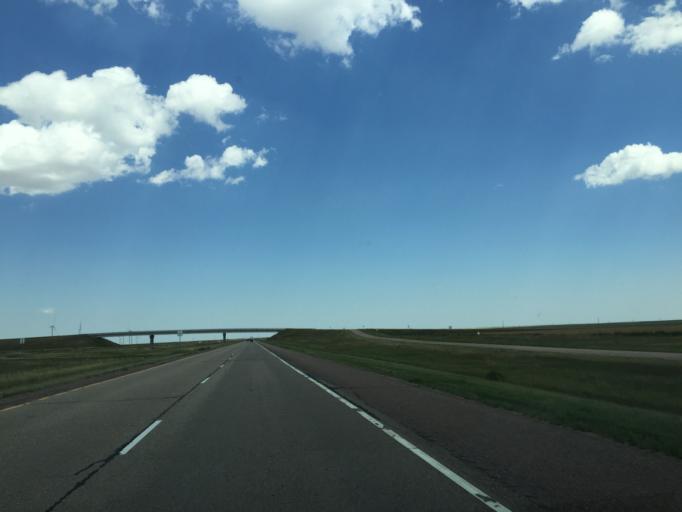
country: US
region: Colorado
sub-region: Lincoln County
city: Hugo
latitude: 39.2778
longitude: -103.4401
